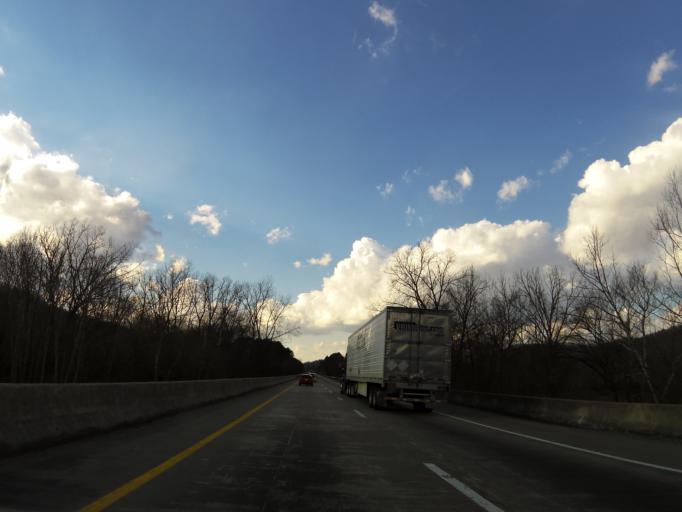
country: US
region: Tennessee
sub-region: Smith County
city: Gordonsville
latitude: 36.1506
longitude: -85.8724
